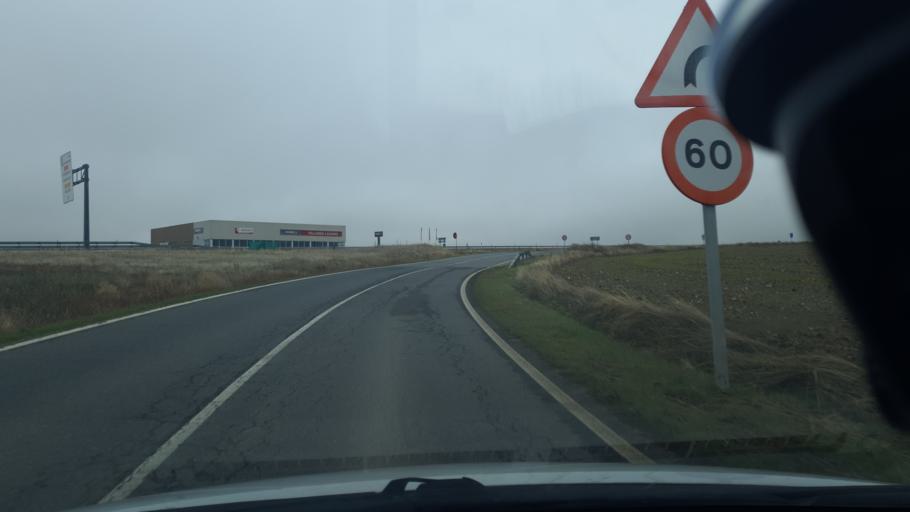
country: ES
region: Castille and Leon
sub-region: Provincia de Segovia
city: Encinillas
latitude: 41.0047
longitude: -4.1590
